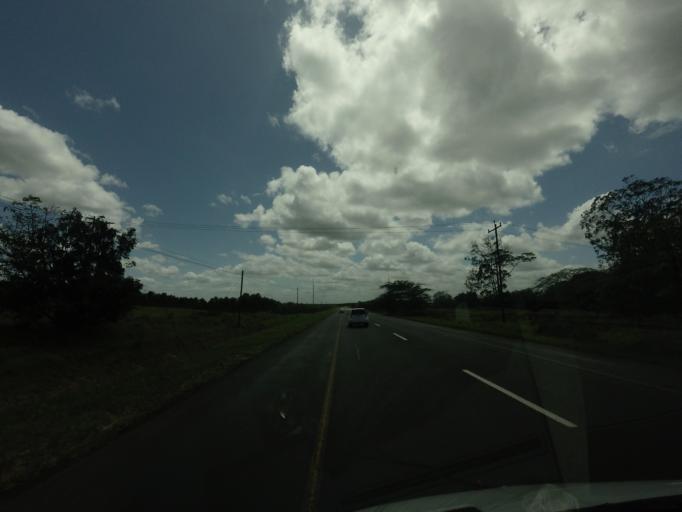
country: ZA
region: KwaZulu-Natal
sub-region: uThungulu District Municipality
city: KwaMbonambi
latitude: -28.5751
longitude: 32.1066
